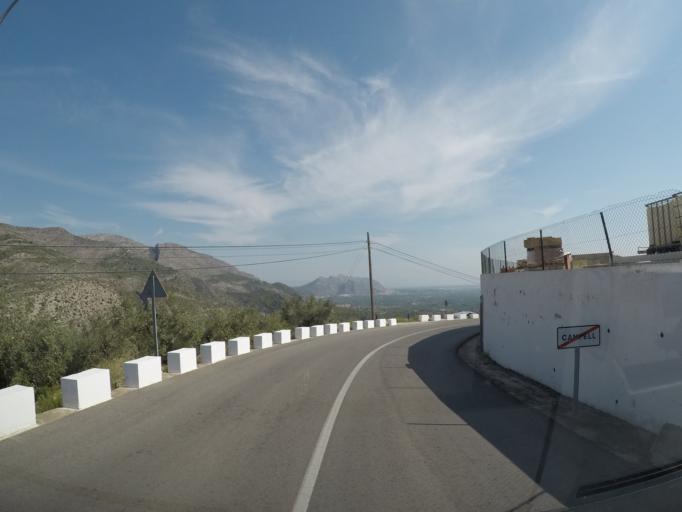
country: ES
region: Valencia
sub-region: Provincia de Alicante
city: Murla
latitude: 38.7812
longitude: -0.1013
